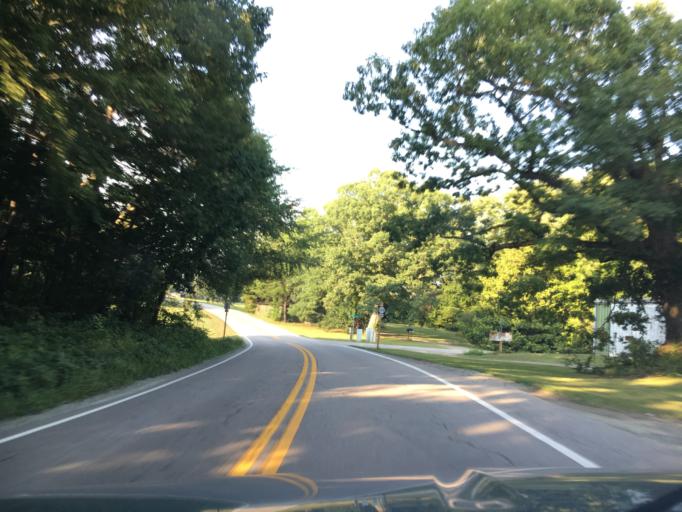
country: US
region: Virginia
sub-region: Pittsylvania County
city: Chatham
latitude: 36.8358
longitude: -79.2283
